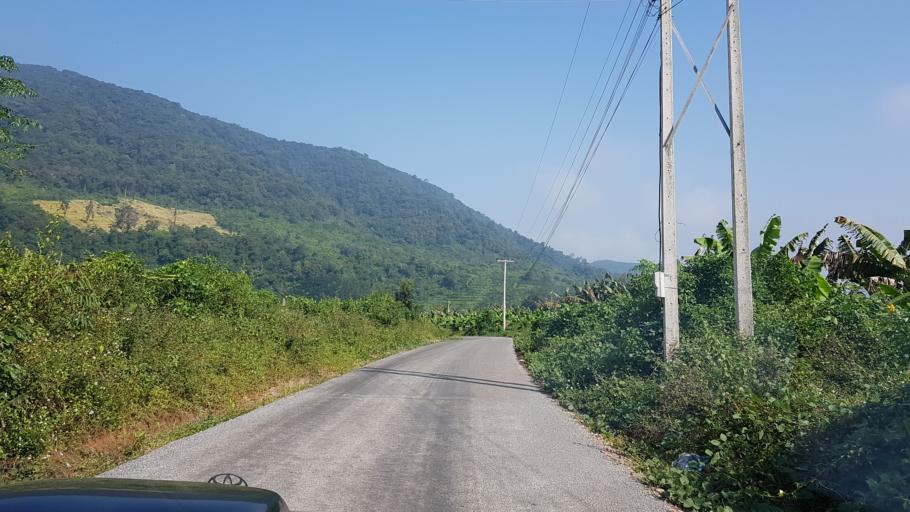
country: LA
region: Oudomxai
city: Muang Xay
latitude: 20.7137
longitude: 102.0781
